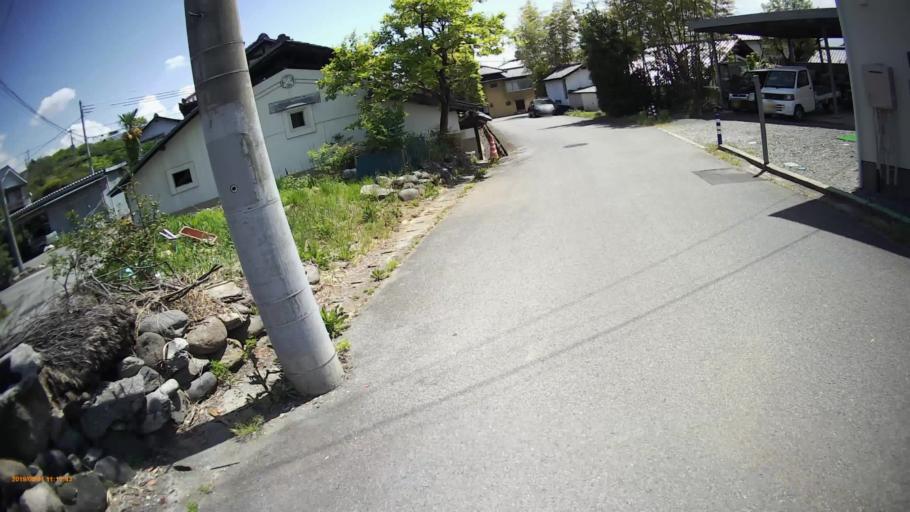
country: JP
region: Yamanashi
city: Nirasaki
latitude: 35.6964
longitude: 138.4710
